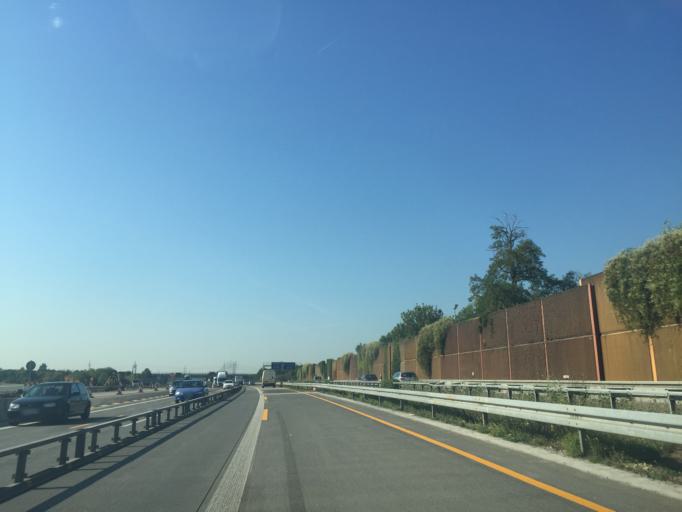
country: DE
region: Baden-Wuerttemberg
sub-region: Karlsruhe Region
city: Eppelheim
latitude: 49.3750
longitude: 8.6326
